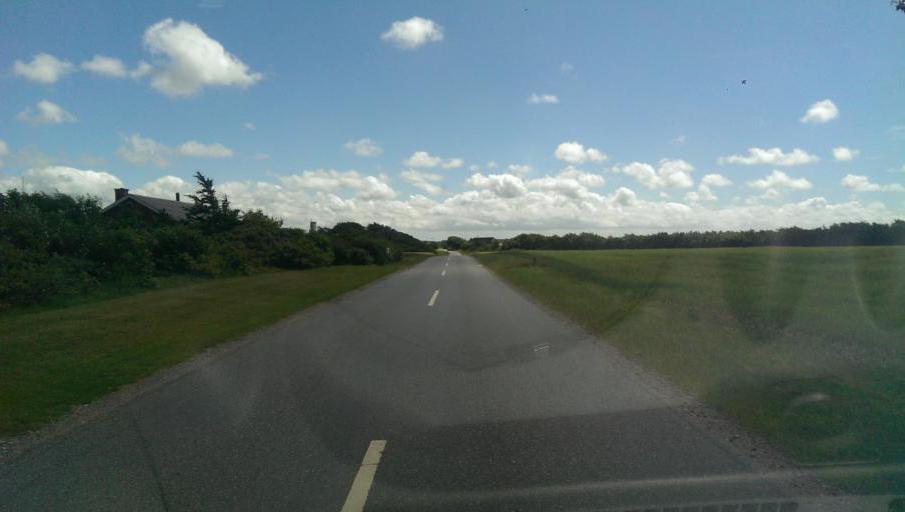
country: DK
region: Central Jutland
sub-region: Holstebro Kommune
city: Ulfborg
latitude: 56.2409
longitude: 8.1892
